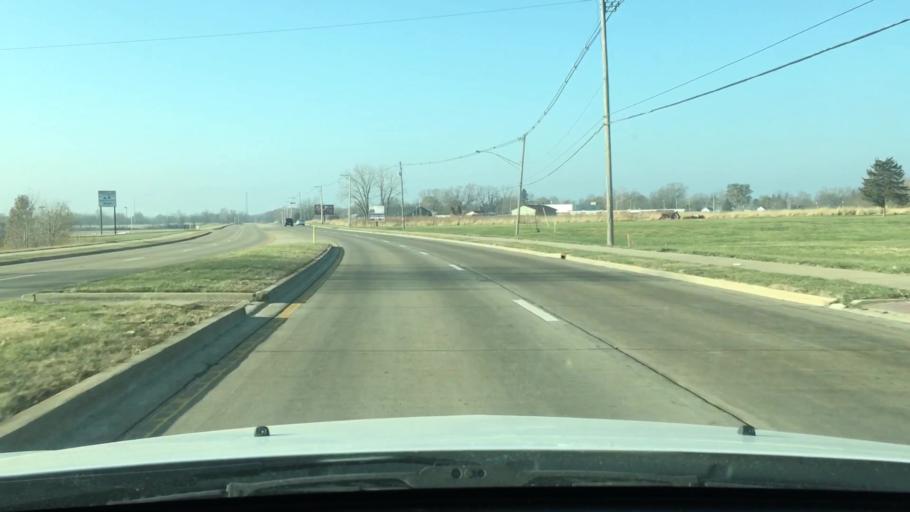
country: US
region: Illinois
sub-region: Tazewell County
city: East Peoria
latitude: 40.6896
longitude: -89.5030
